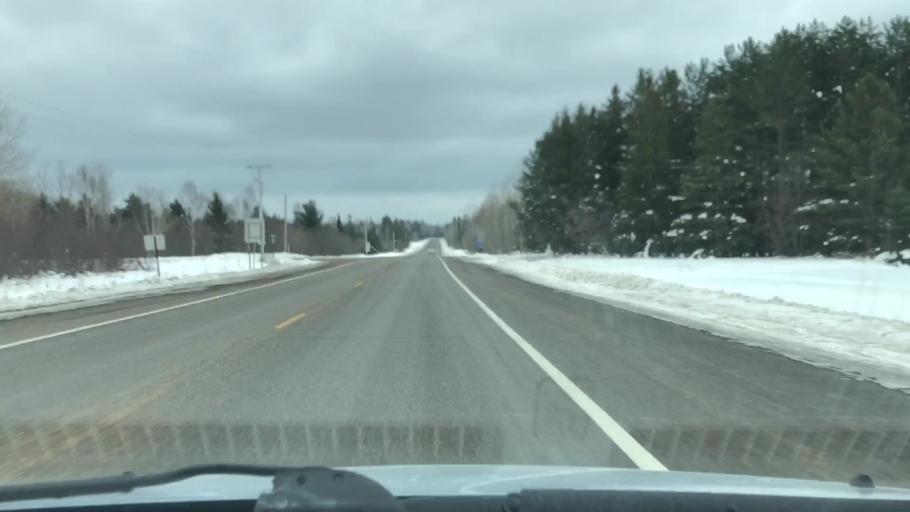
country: US
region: Minnesota
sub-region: Carlton County
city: Esko
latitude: 46.6931
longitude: -92.3650
